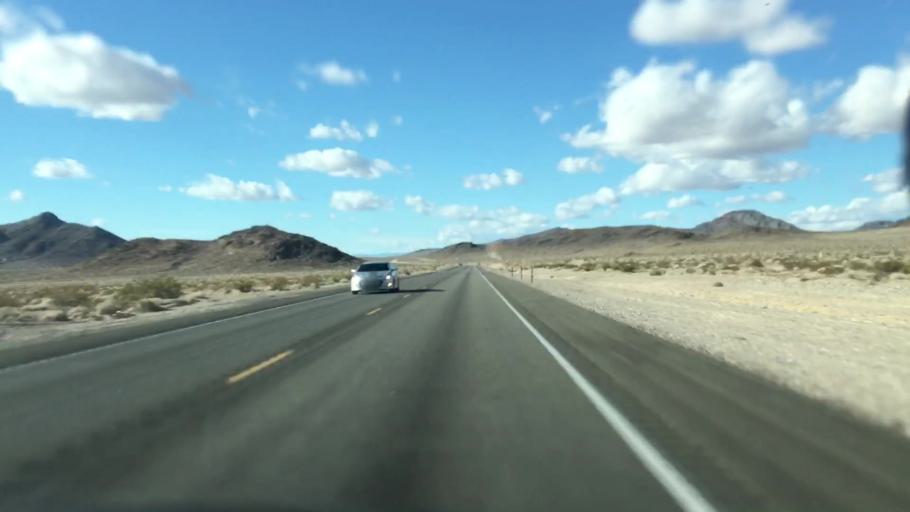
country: US
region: Nevada
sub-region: Nye County
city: Pahrump
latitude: 36.6204
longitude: -116.2926
